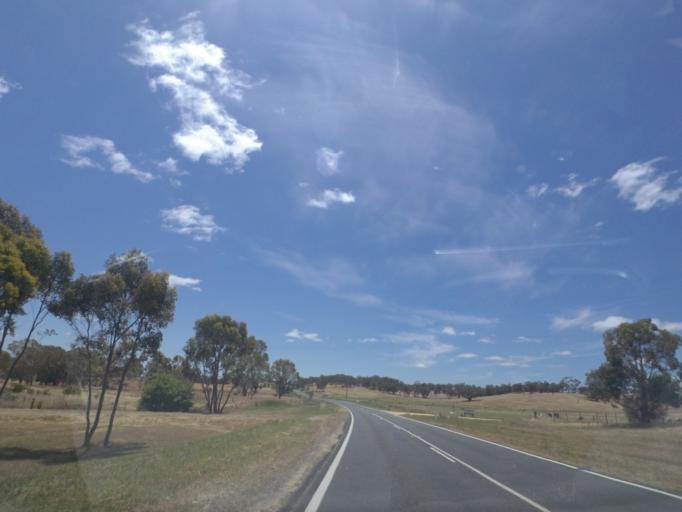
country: AU
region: Victoria
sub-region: Mount Alexander
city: Castlemaine
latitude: -37.2202
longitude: 144.1408
